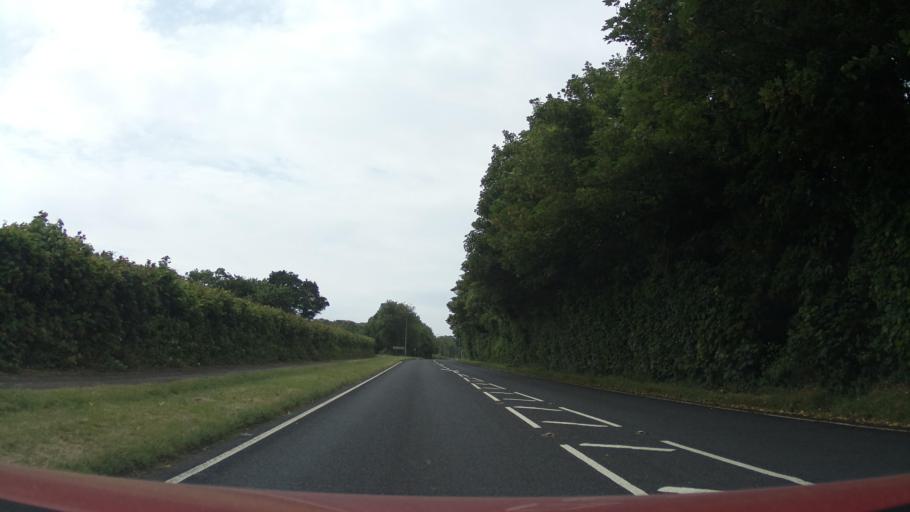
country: GB
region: Wales
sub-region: Vale of Glamorgan
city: Penarth
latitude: 51.4126
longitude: -3.1842
